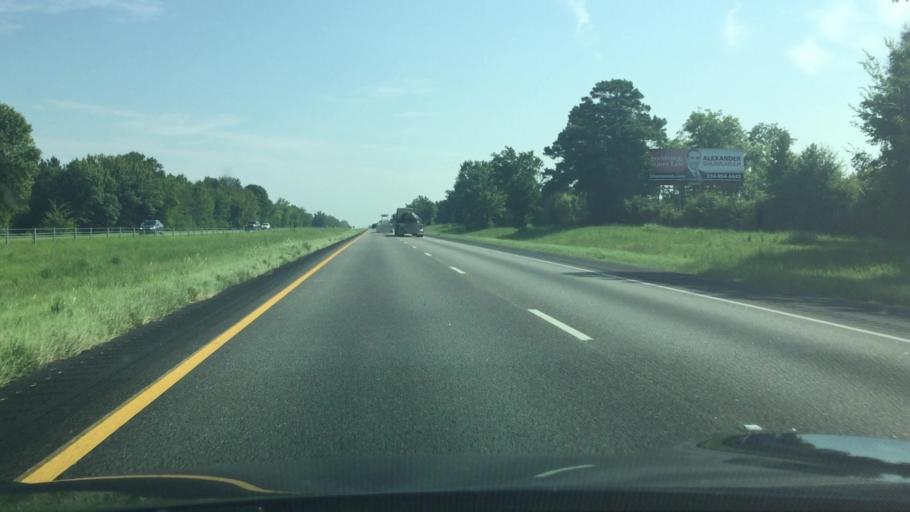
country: US
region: Alabama
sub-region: Montgomery County
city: Montgomery
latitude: 32.2437
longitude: -86.3731
